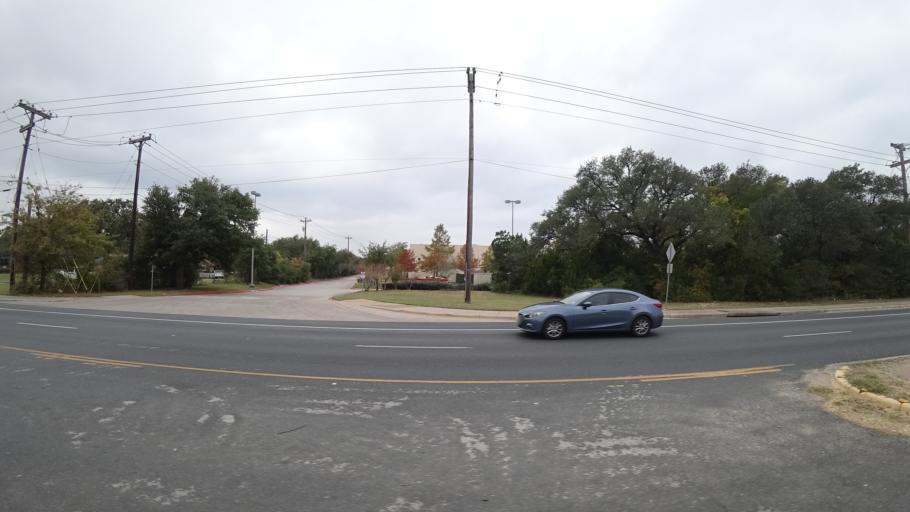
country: US
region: Texas
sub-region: Williamson County
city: Anderson Mill
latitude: 30.4543
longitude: -97.8240
